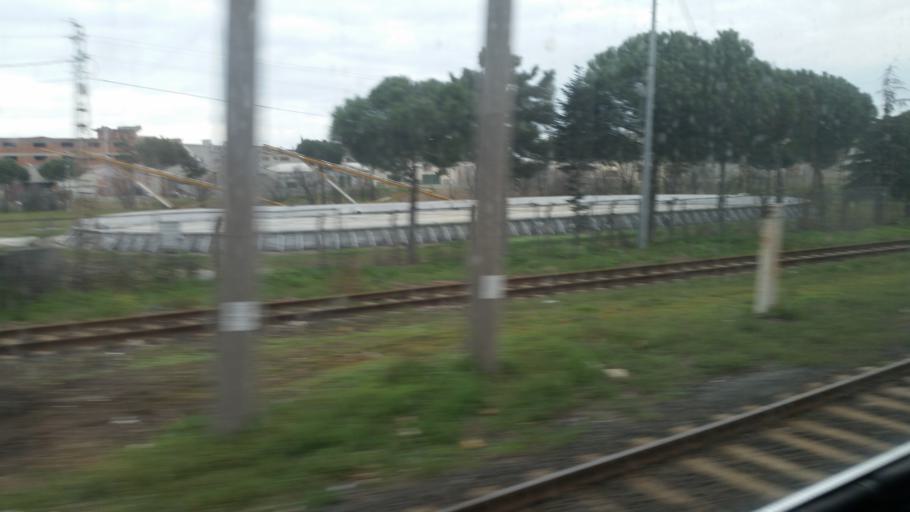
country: TR
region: Tekirdag
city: Corlu
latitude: 41.1777
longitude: 27.7793
